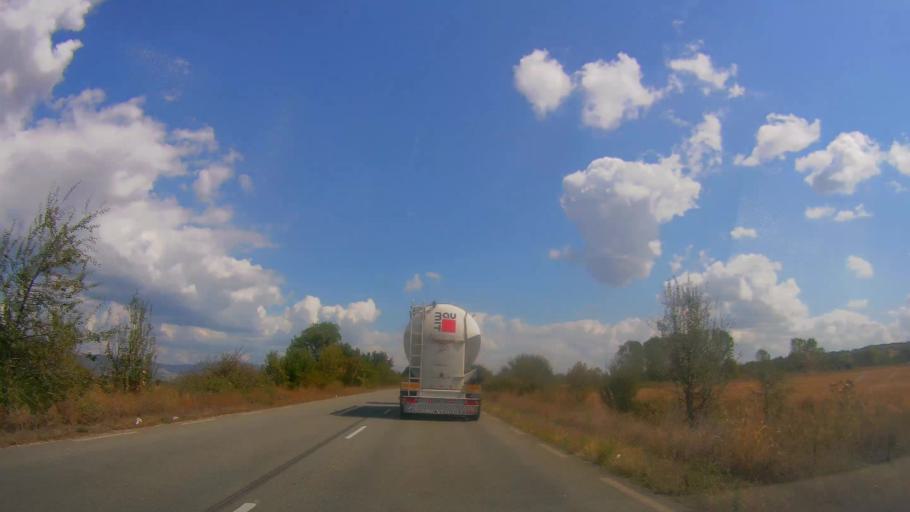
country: BG
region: Sliven
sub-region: Obshtina Tvurditsa
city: Tvurditsa
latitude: 42.6571
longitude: 25.9234
